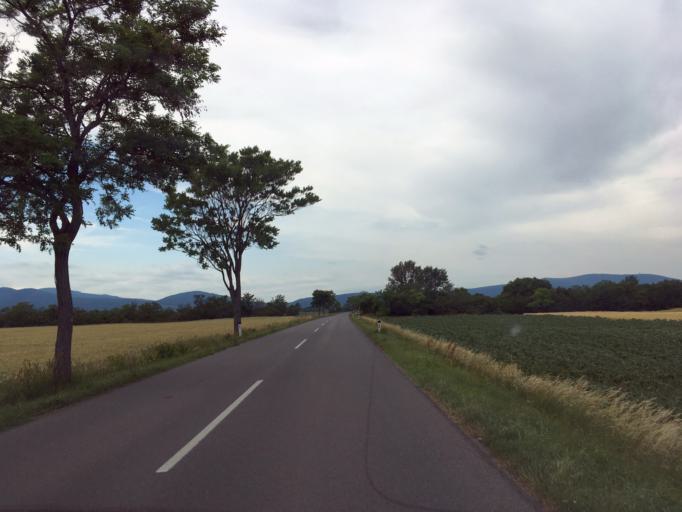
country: AT
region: Lower Austria
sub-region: Politischer Bezirk Baden
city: Teesdorf
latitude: 47.9565
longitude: 16.2753
